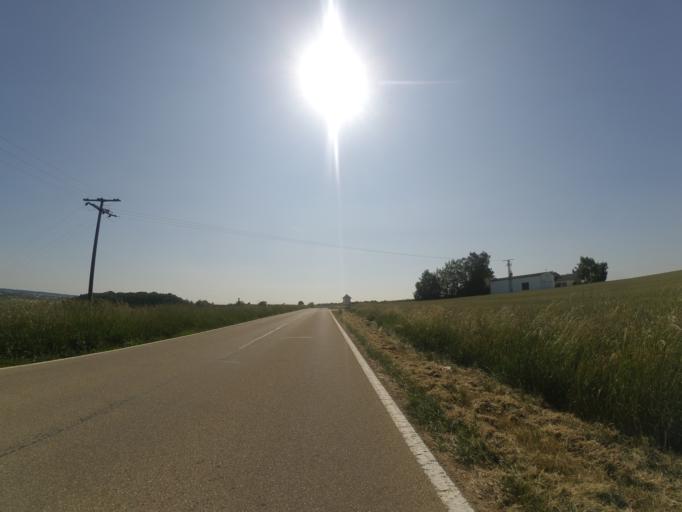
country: DE
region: Baden-Wuerttemberg
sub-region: Tuebingen Region
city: Beimerstetten
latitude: 48.4820
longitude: 9.9973
